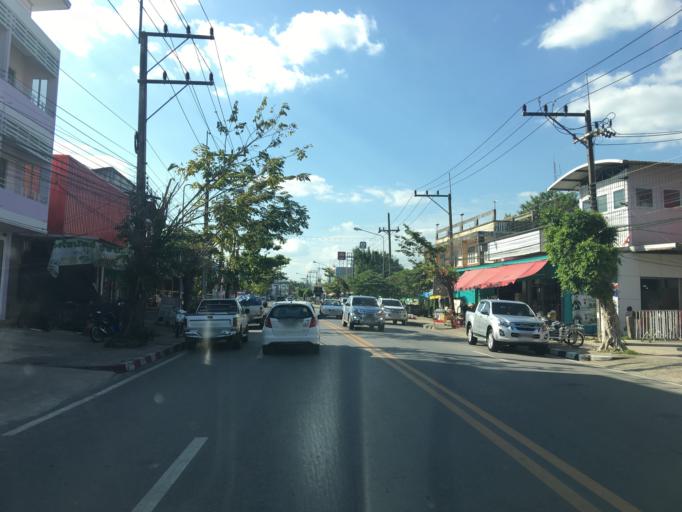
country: TH
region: Phayao
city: Chun
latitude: 19.3410
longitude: 100.1244
